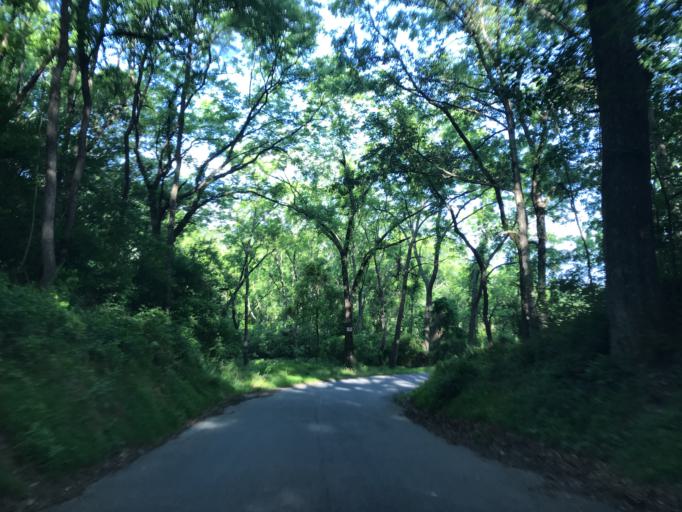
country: US
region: Maryland
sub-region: Baltimore County
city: Reisterstown
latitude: 39.5243
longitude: -76.8511
